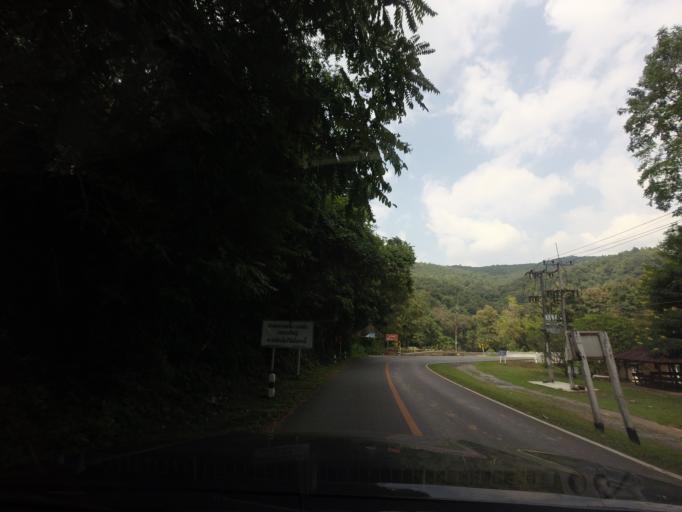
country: TH
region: Nan
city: Pua
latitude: 19.1796
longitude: 100.9587
